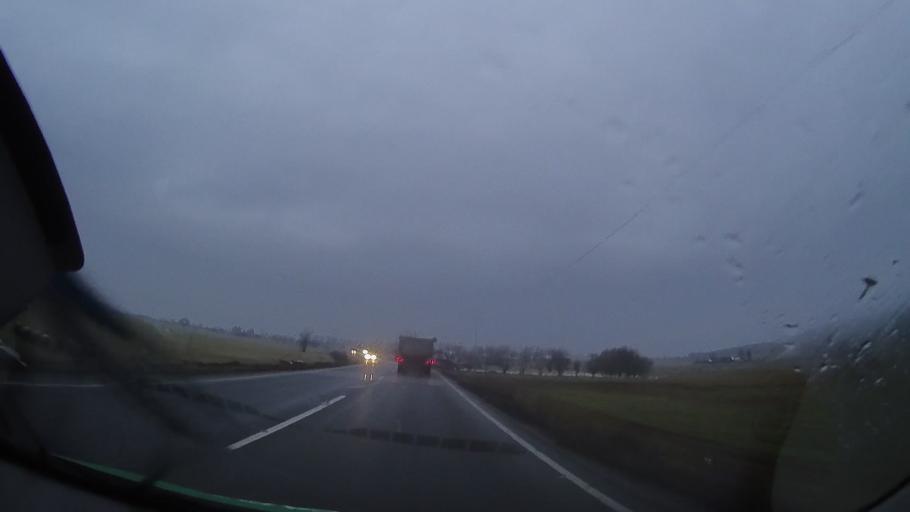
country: RO
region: Harghita
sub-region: Comuna Lazarea
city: Lazarea
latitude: 46.7593
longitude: 25.5164
